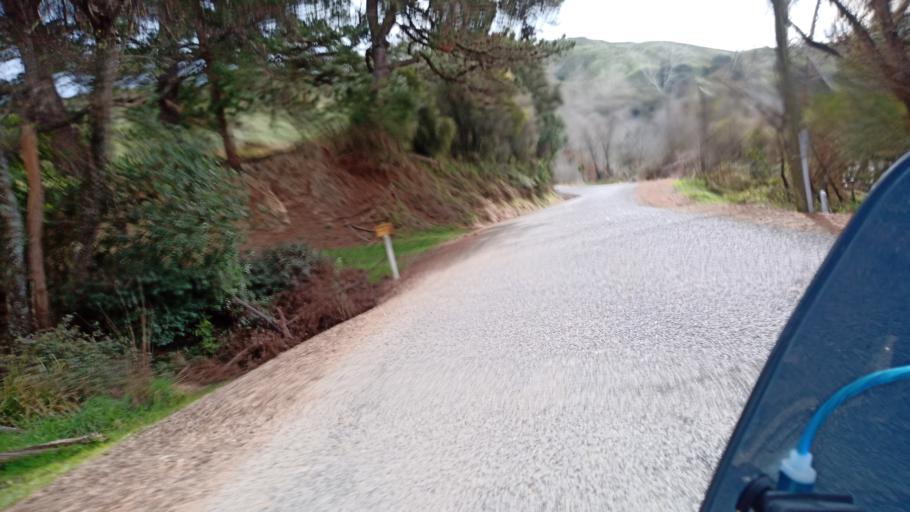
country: NZ
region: Hawke's Bay
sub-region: Wairoa District
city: Wairoa
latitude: -38.7929
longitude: 177.4346
